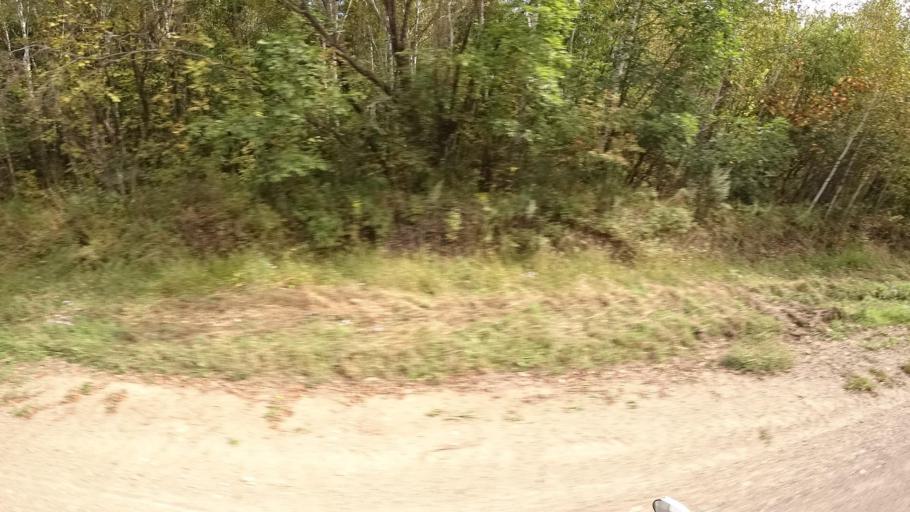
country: RU
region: Primorskiy
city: Yakovlevka
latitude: 44.7443
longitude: 133.6063
